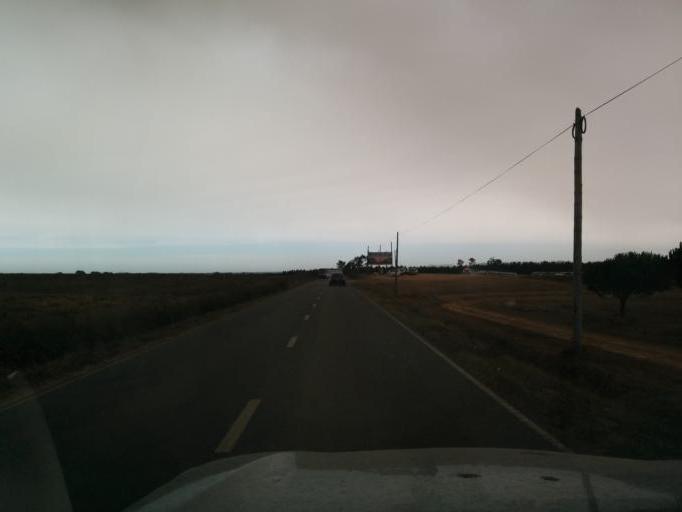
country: PT
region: Beja
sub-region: Odemira
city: Sao Teotonio
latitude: 37.5524
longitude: -8.7345
